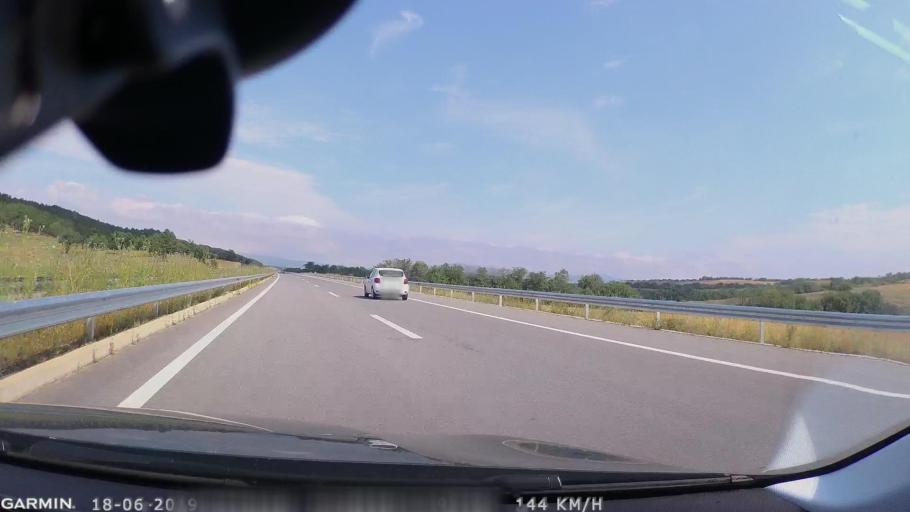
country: MK
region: Sveti Nikole
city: Sveti Nikole
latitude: 41.8926
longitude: 21.9264
